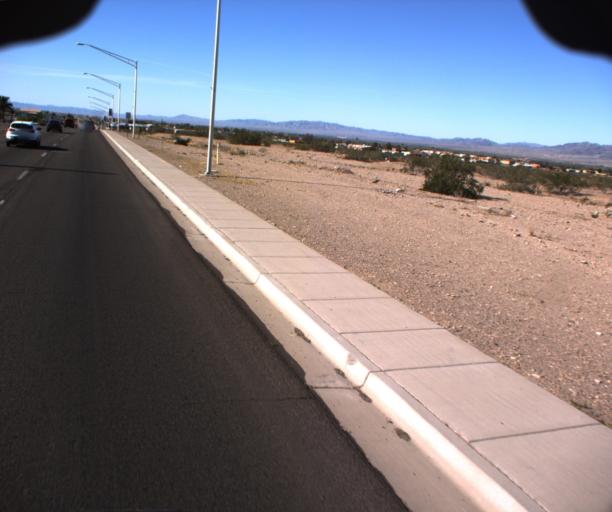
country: US
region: Arizona
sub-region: Mohave County
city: Bullhead City
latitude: 35.0991
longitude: -114.5981
